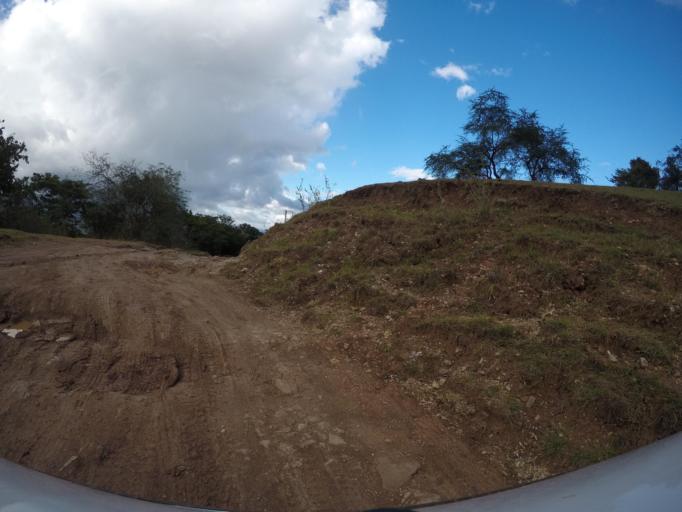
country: TL
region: Baucau
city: Venilale
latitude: -8.6874
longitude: 126.6619
